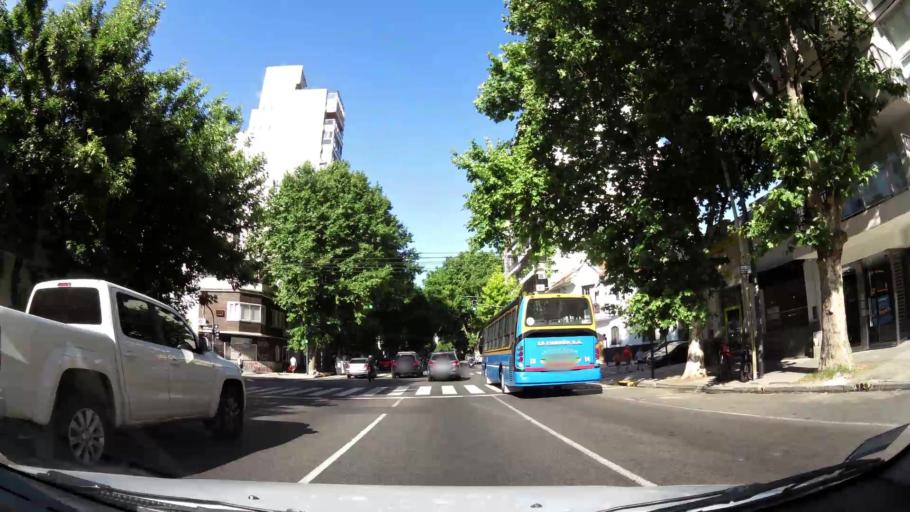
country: AR
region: Buenos Aires F.D.
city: Villa Santa Rita
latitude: -34.6221
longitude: -58.4585
